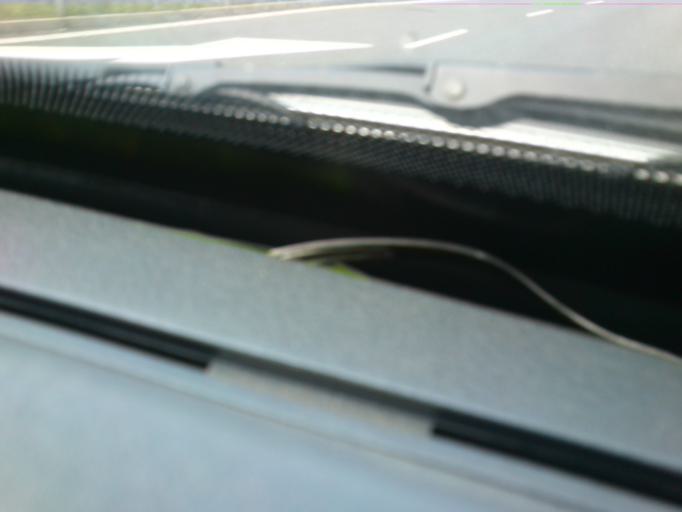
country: CZ
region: Praha
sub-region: Praha 9
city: Strizkov
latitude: 50.1389
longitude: 14.4928
